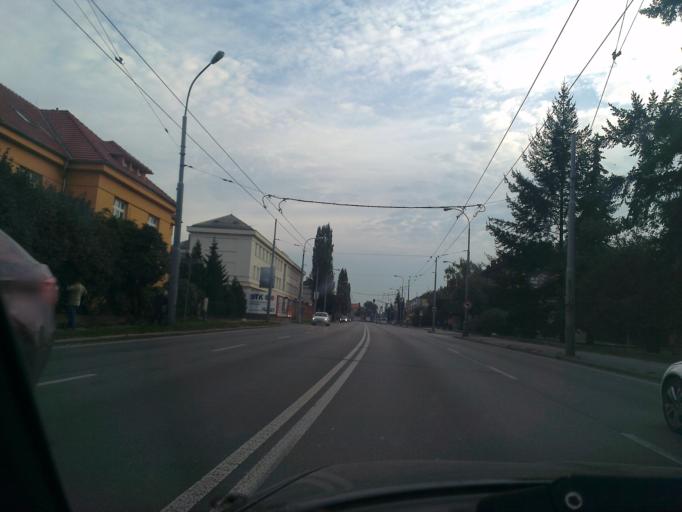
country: CZ
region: South Moravian
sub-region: Mesto Brno
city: Brno
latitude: 49.2094
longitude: 16.6425
